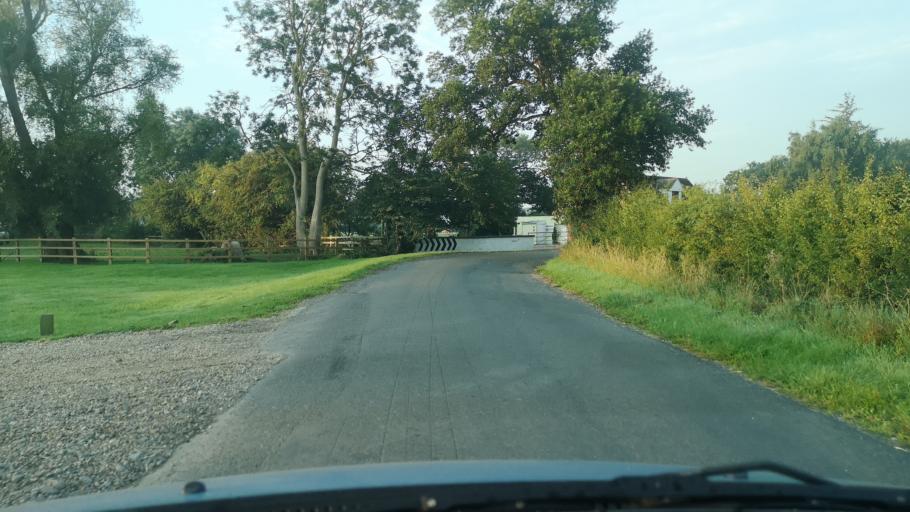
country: GB
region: England
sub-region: Doncaster
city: Stainforth
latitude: 53.6139
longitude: -1.0627
